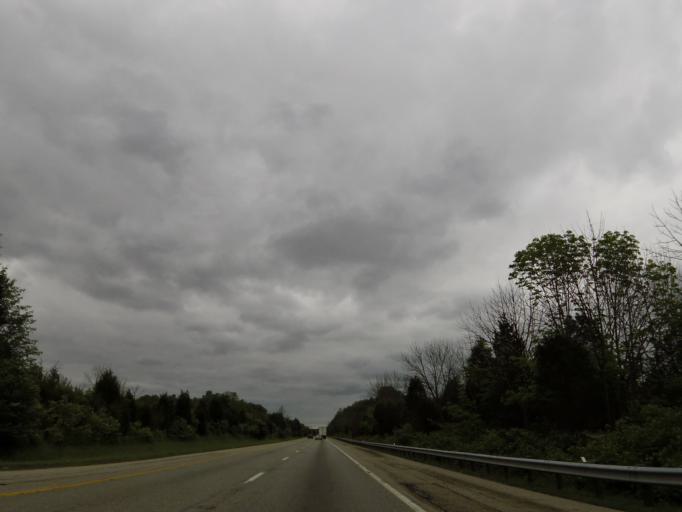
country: US
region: Ohio
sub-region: Warren County
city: South Lebanon
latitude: 39.3914
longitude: -84.1996
